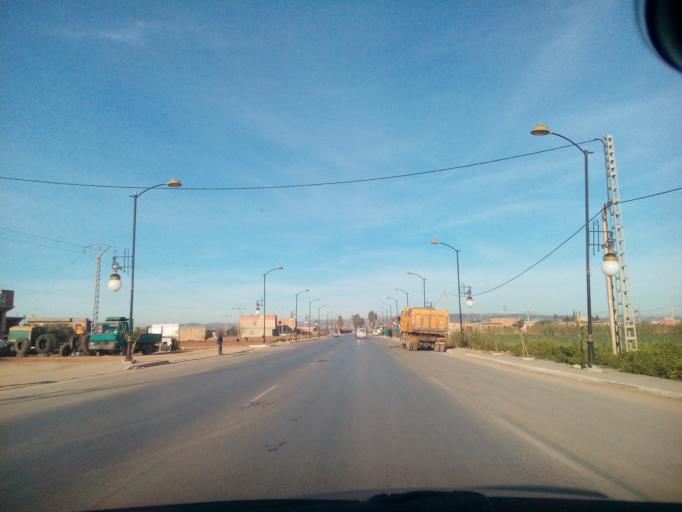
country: DZ
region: Mostaganem
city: Mostaganem
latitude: 35.7839
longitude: 0.1812
